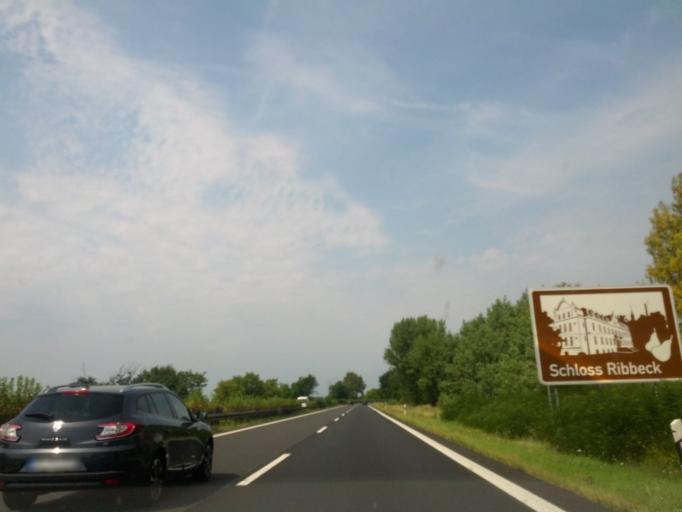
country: DE
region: Brandenburg
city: Wustermark
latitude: 52.5072
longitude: 12.9605
